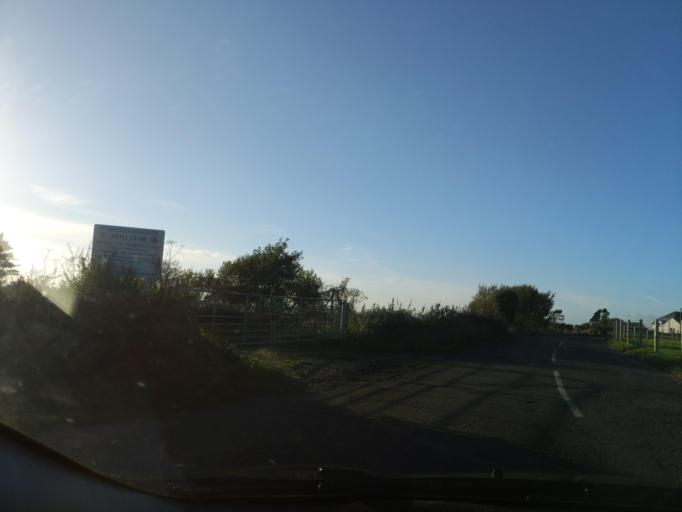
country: GB
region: England
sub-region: Plymouth
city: Plymstock
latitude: 50.3446
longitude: -4.1152
